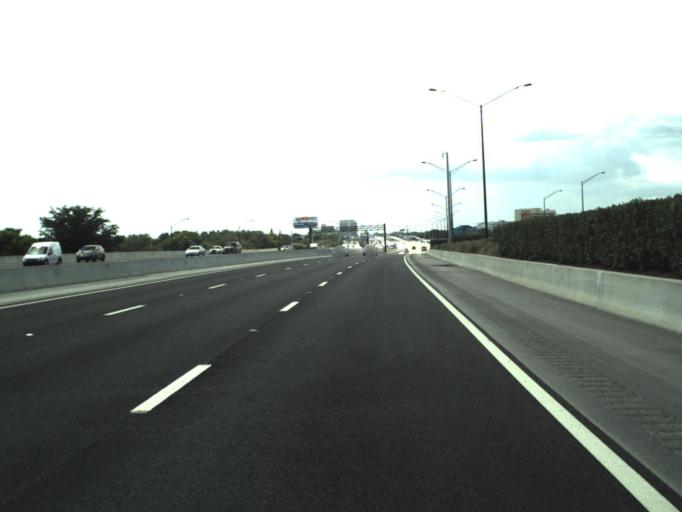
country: US
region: Florida
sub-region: Broward County
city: Pine Island Ridge
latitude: 26.0990
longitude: -80.2517
